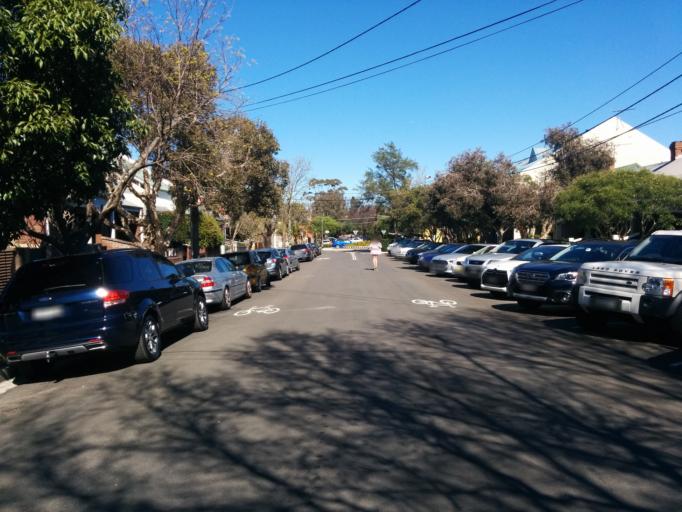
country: AU
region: New South Wales
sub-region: City of Sydney
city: Alexandria
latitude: -33.9046
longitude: 151.1910
